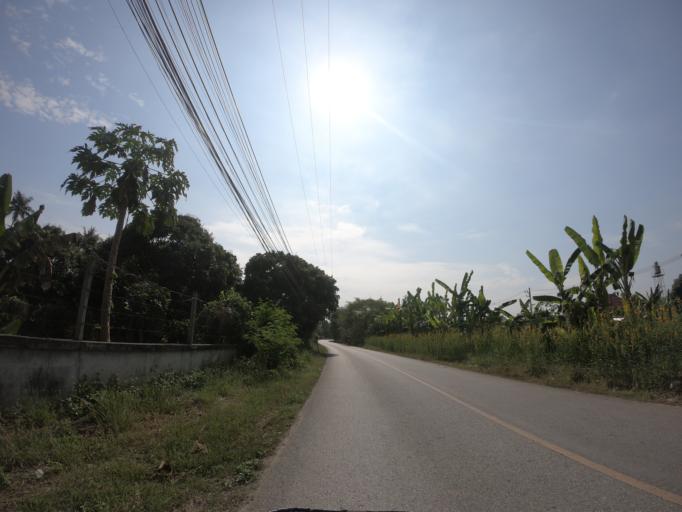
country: TH
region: Chiang Mai
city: Saraphi
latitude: 18.6968
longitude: 99.0586
